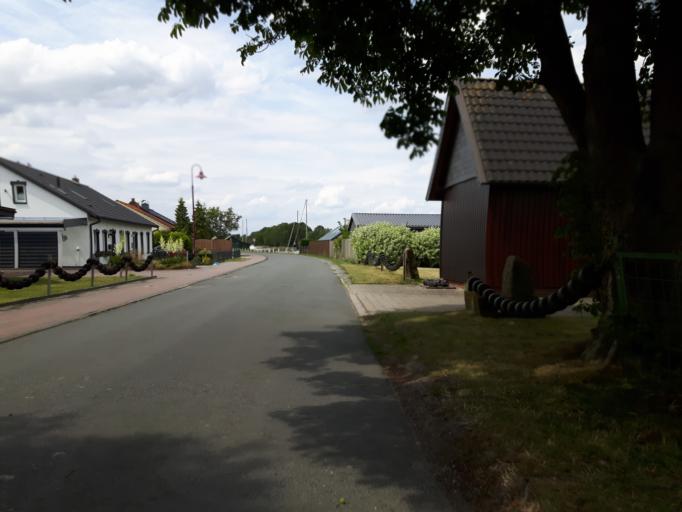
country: DE
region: Lower Saxony
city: Varel
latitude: 53.4079
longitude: 8.1786
